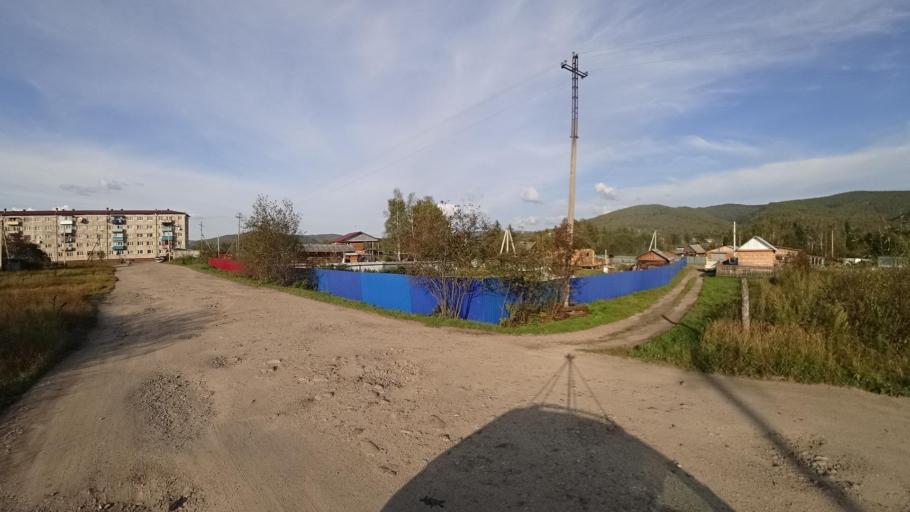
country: RU
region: Jewish Autonomous Oblast
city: Kul'dur
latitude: 49.2000
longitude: 131.6261
